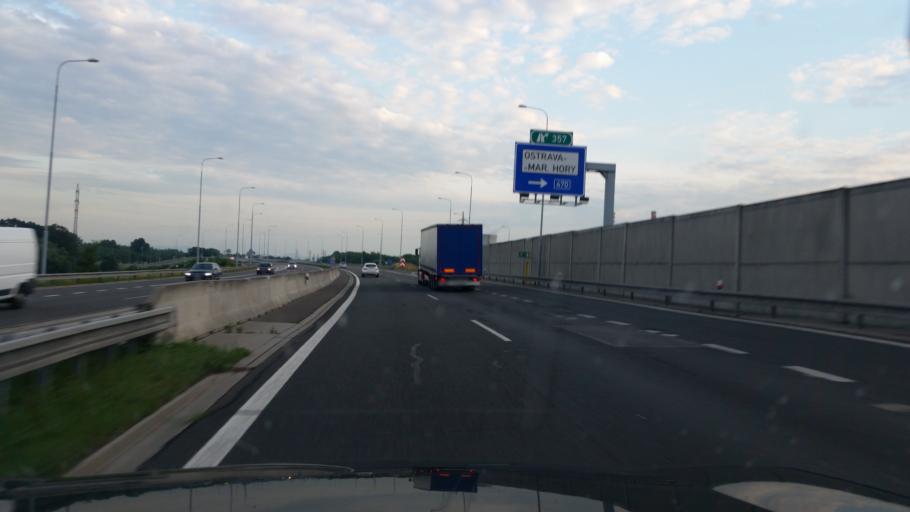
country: CZ
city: Ludgerovice
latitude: 49.8395
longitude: 18.2192
